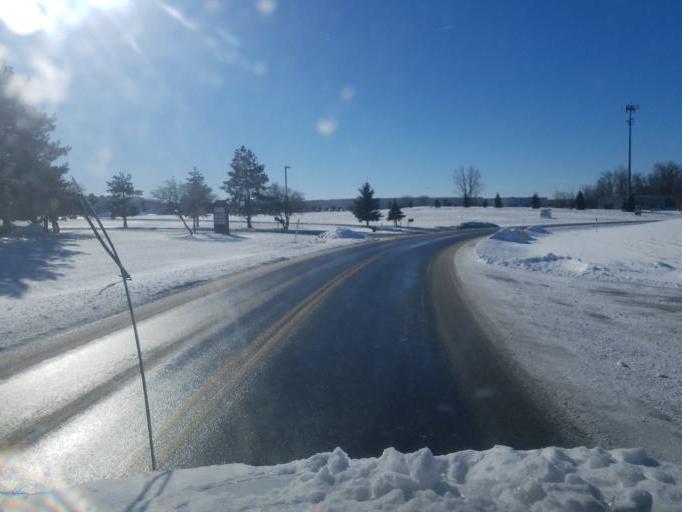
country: US
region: Ohio
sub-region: Delaware County
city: Lewis Center
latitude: 40.1629
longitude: -83.0095
